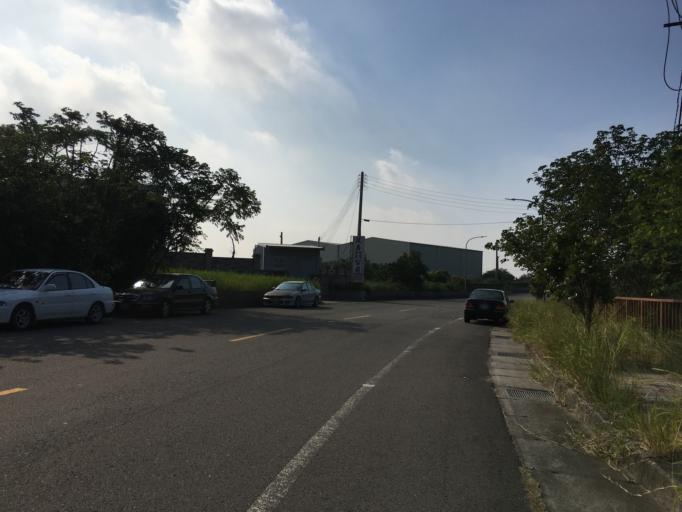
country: TW
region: Taiwan
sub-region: Hsinchu
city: Hsinchu
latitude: 24.8037
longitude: 120.9177
